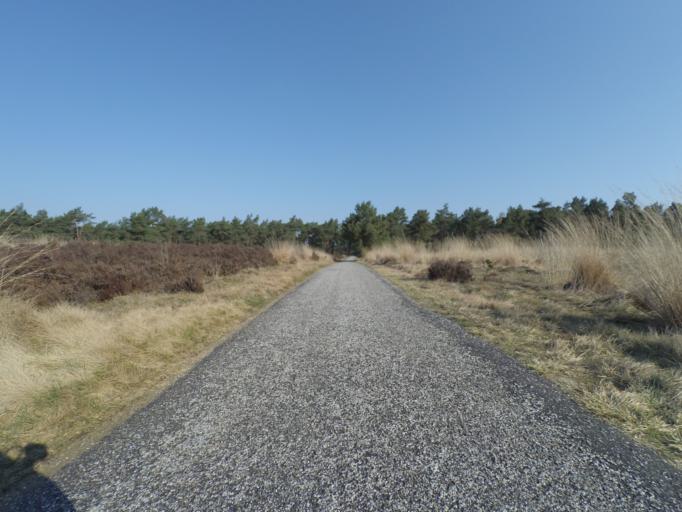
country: NL
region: Gelderland
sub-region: Gemeente Arnhem
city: Hoogkamp
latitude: 52.0680
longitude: 5.8463
